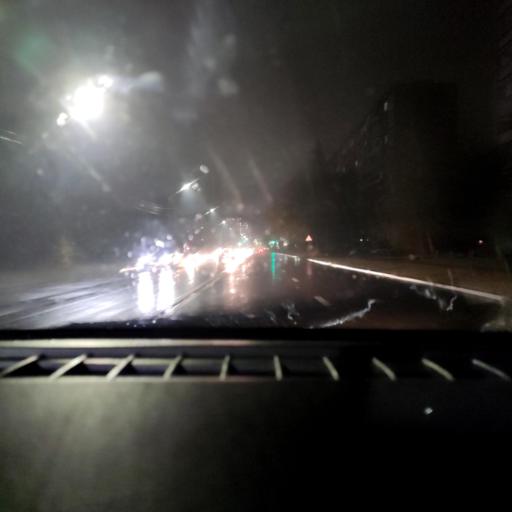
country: RU
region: Voronezj
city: Maslovka
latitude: 51.5969
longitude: 39.2437
